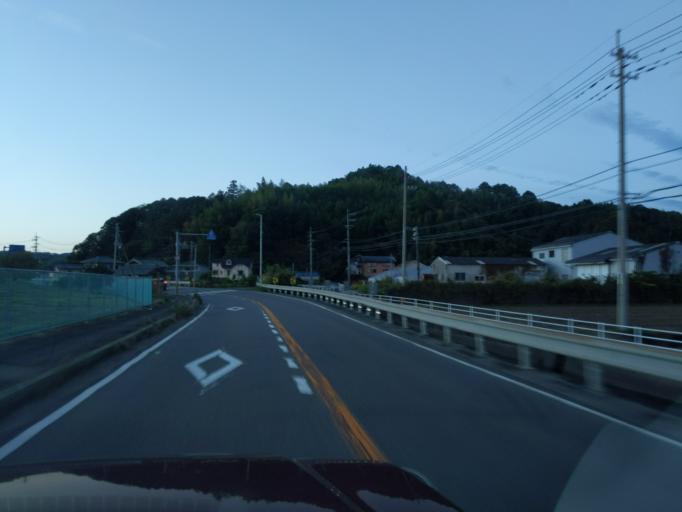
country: JP
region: Tokushima
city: Anan
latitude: 33.8586
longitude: 134.6267
